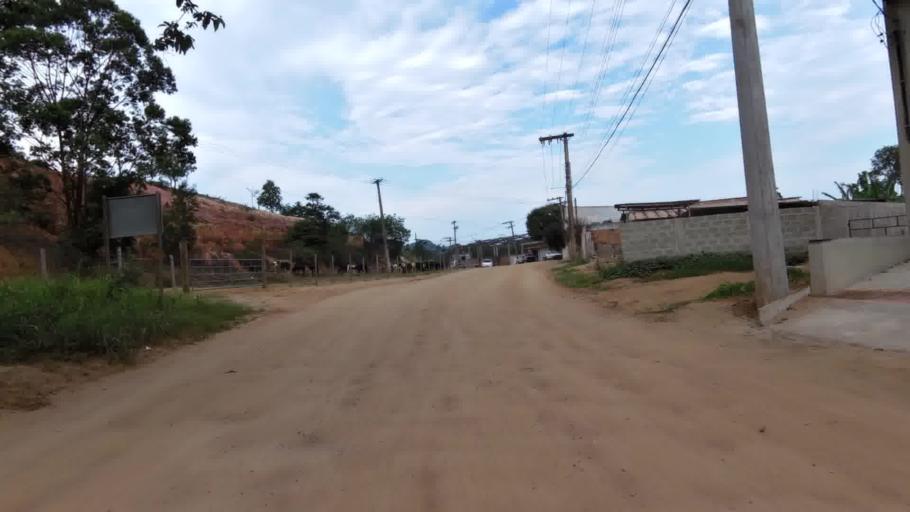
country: BR
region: Espirito Santo
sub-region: Piuma
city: Piuma
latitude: -20.8347
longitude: -40.7296
